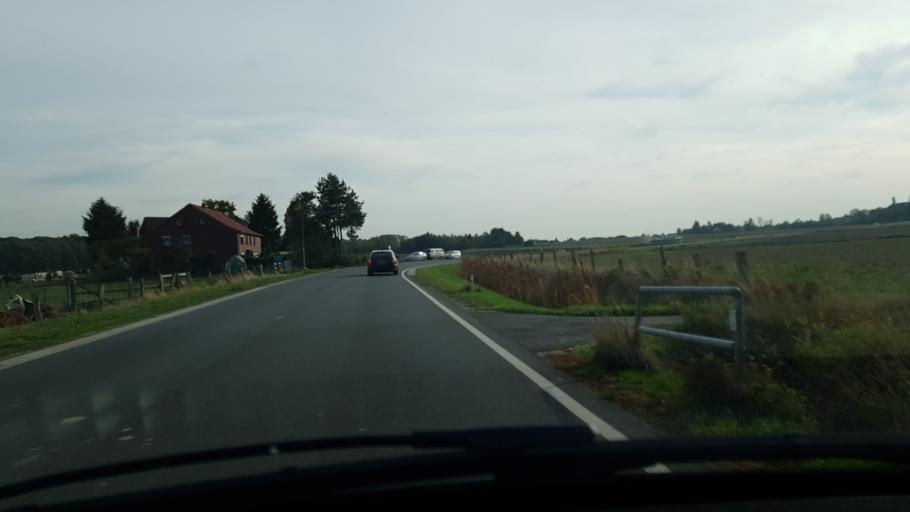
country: DE
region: Lower Saxony
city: Lehre
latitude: 52.3040
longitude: 10.6597
